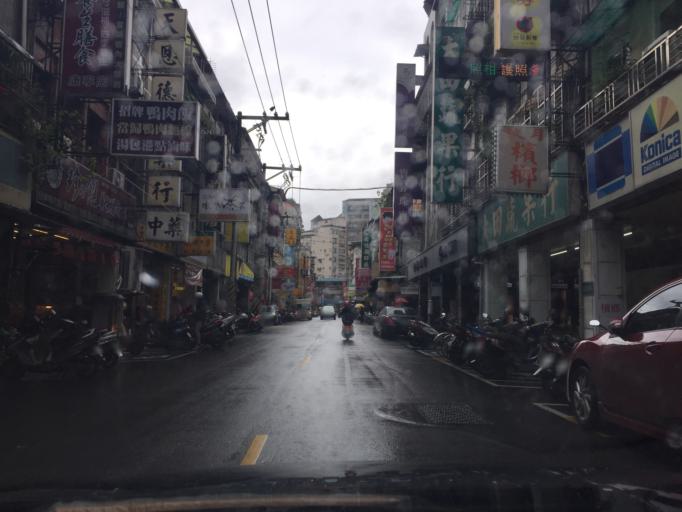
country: TW
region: Taipei
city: Taipei
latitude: 25.0800
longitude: 121.5926
